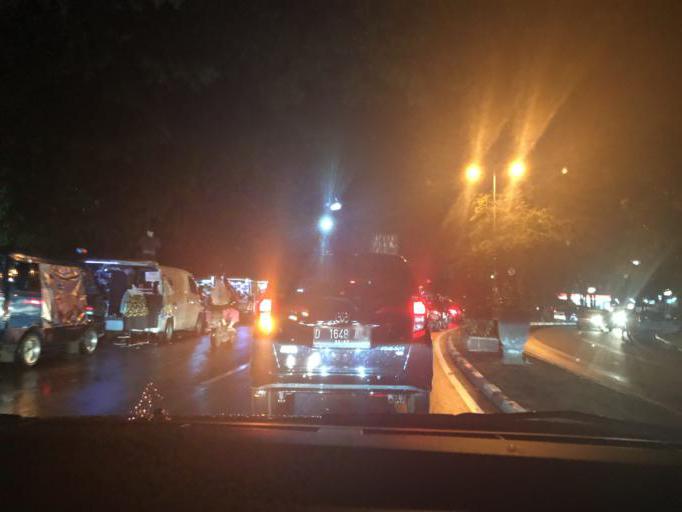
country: ID
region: West Java
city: Bandung
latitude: -6.9010
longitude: 107.6259
